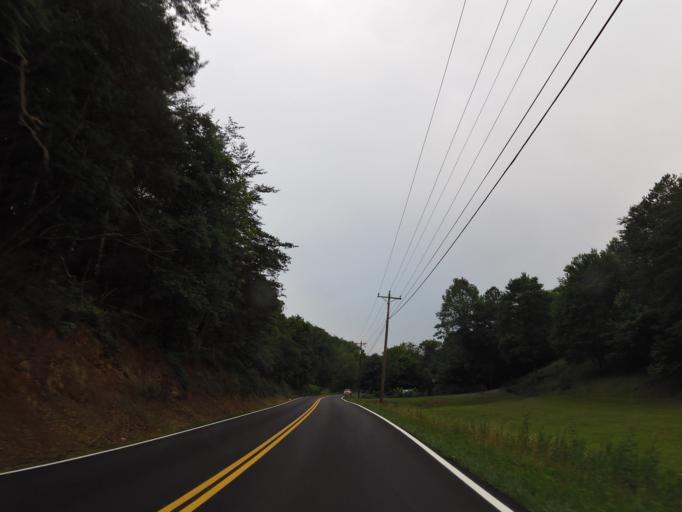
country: US
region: Tennessee
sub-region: Sevier County
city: Pigeon Forge
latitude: 35.8064
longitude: -83.6216
